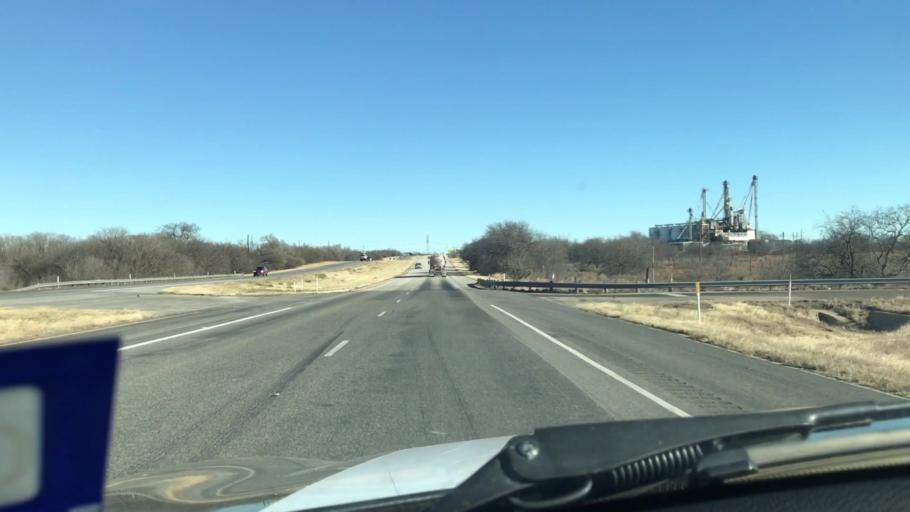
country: US
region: Texas
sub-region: Scurry County
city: Snyder
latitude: 32.6871
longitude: -100.8497
